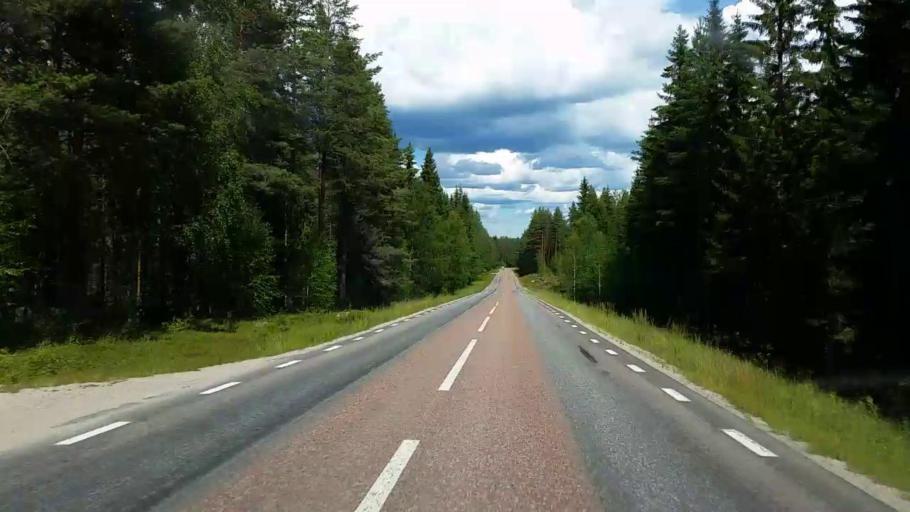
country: SE
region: Gaevleborg
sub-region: Ovanakers Kommun
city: Edsbyn
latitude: 61.3259
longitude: 15.5199
